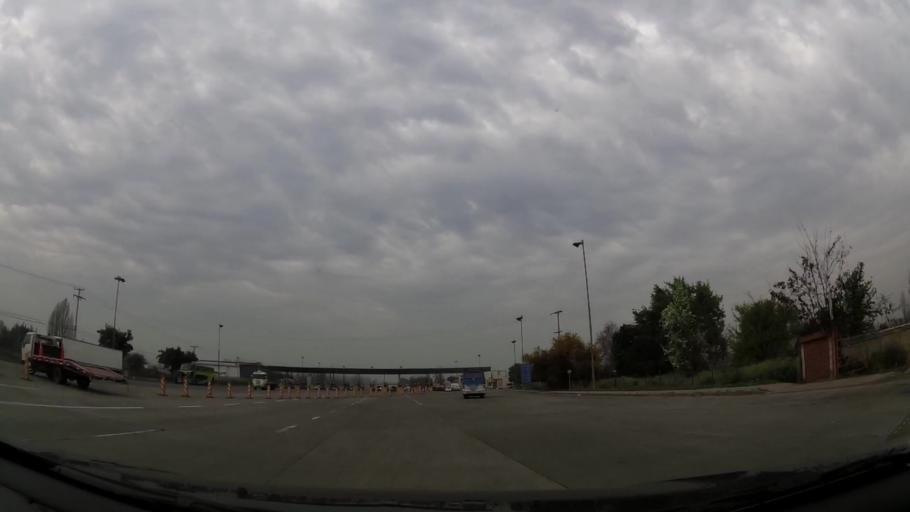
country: CL
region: Santiago Metropolitan
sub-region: Provincia de Chacabuco
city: Chicureo Abajo
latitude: -33.2344
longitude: -70.7596
